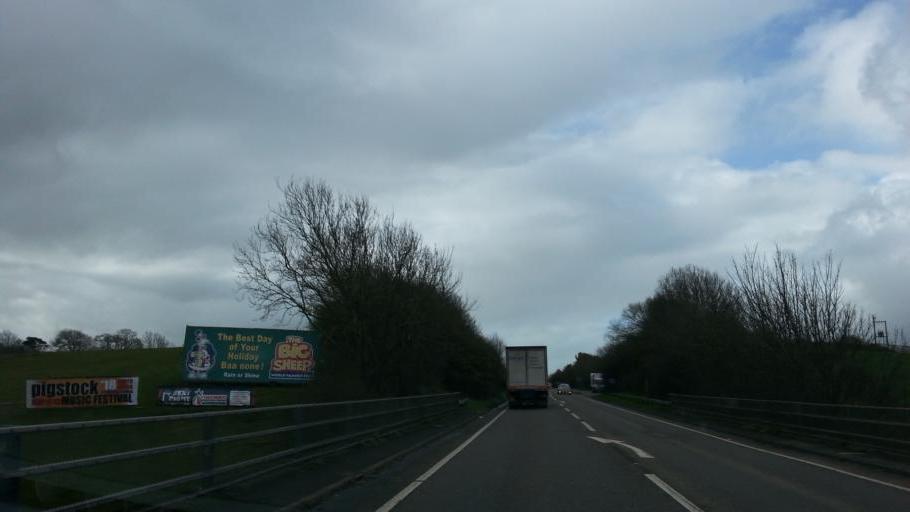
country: GB
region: England
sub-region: Devon
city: Northam
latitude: 51.0222
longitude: -4.2347
